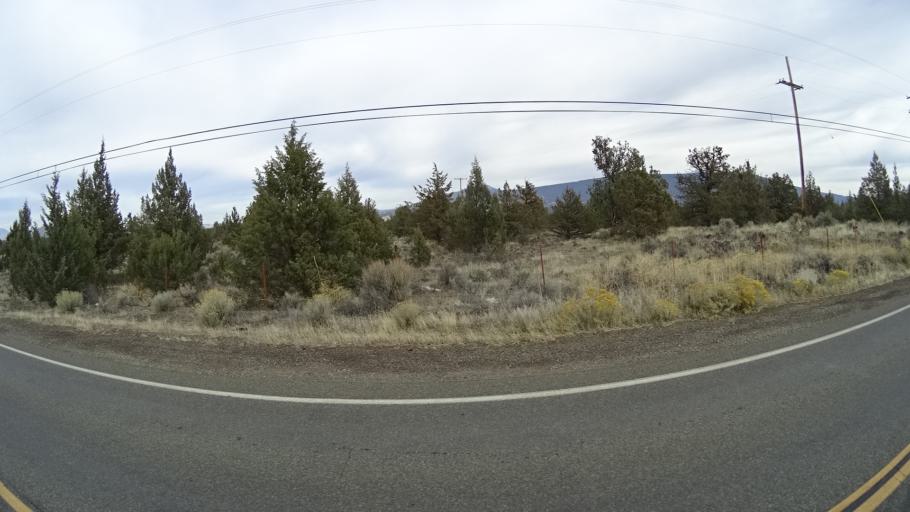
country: US
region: California
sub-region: Siskiyou County
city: Weed
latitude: 41.6060
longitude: -122.3605
